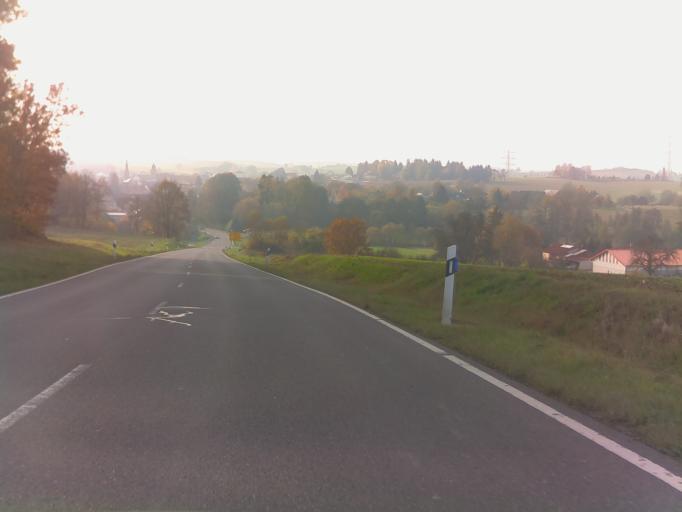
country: DE
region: Baden-Wuerttemberg
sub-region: Karlsruhe Region
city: Seckach
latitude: 49.4198
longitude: 9.2974
